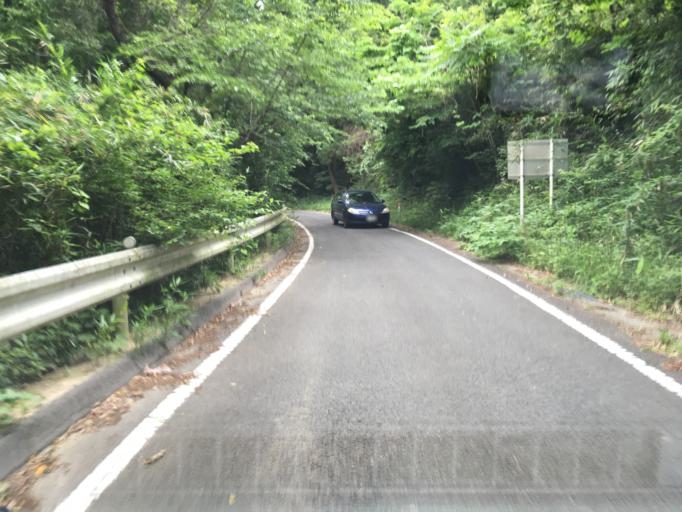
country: JP
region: Fukushima
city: Nihommatsu
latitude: 37.6362
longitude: 140.5261
